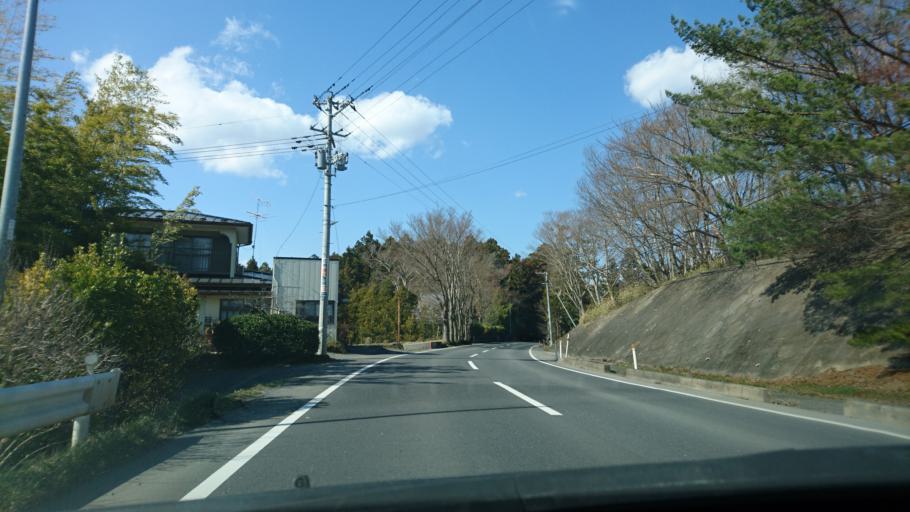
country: JP
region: Iwate
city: Ichinoseki
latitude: 38.7495
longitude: 141.2541
